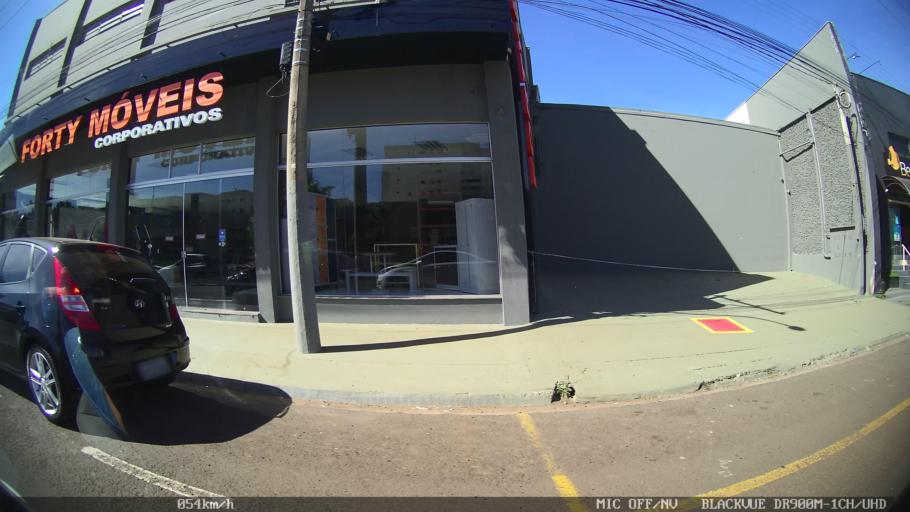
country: BR
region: Sao Paulo
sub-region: Franca
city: Franca
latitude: -20.5447
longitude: -47.3977
